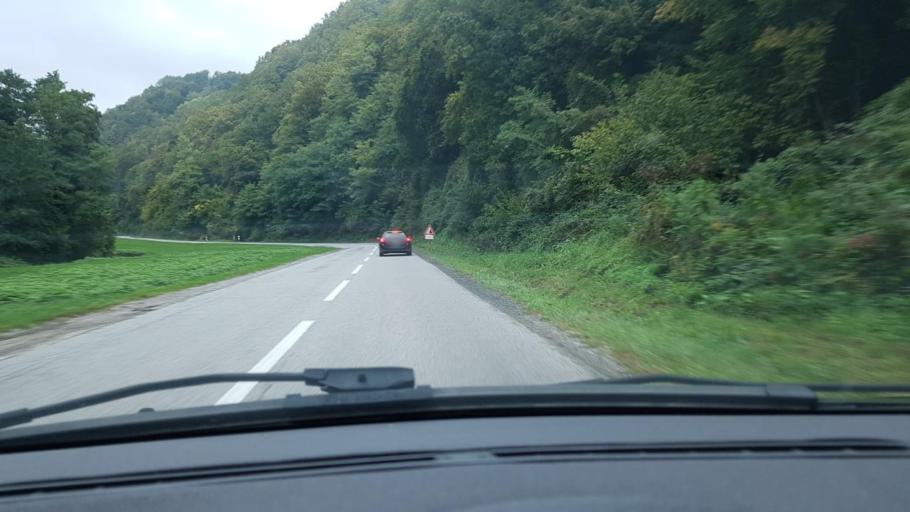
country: HR
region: Krapinsko-Zagorska
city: Marija Bistrica
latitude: 45.9377
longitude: 16.1123
